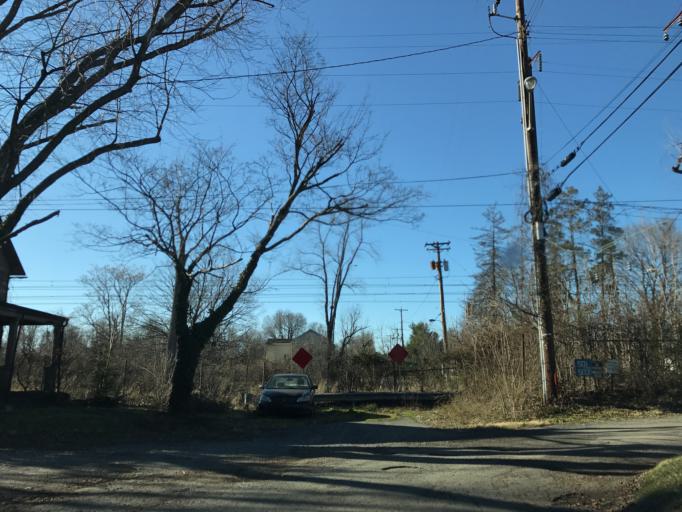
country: US
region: Maryland
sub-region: Harford County
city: Perryman
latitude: 39.4653
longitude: -76.2003
